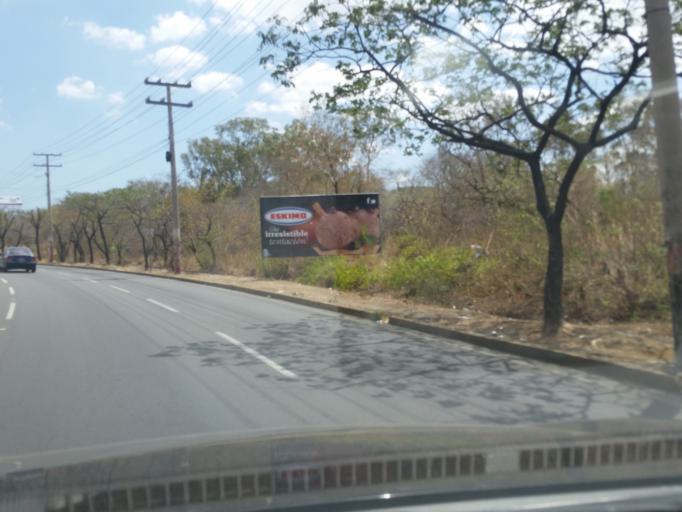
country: NI
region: Managua
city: Managua
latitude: 12.1122
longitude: -86.2756
